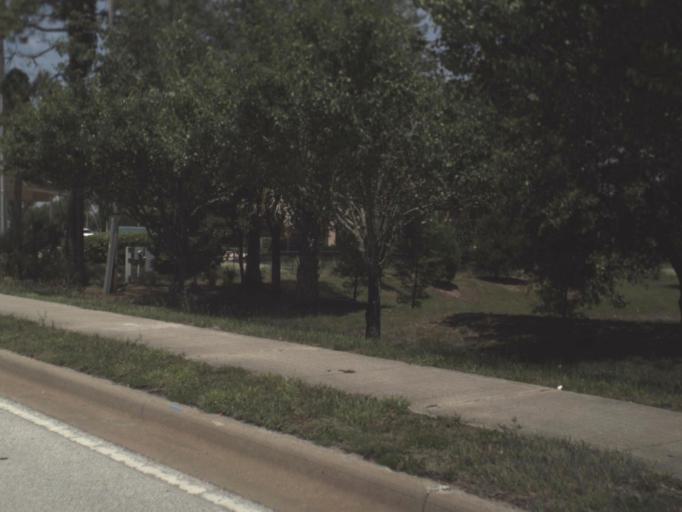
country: US
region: Florida
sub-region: Saint Johns County
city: Fruit Cove
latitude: 30.2186
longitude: -81.5502
